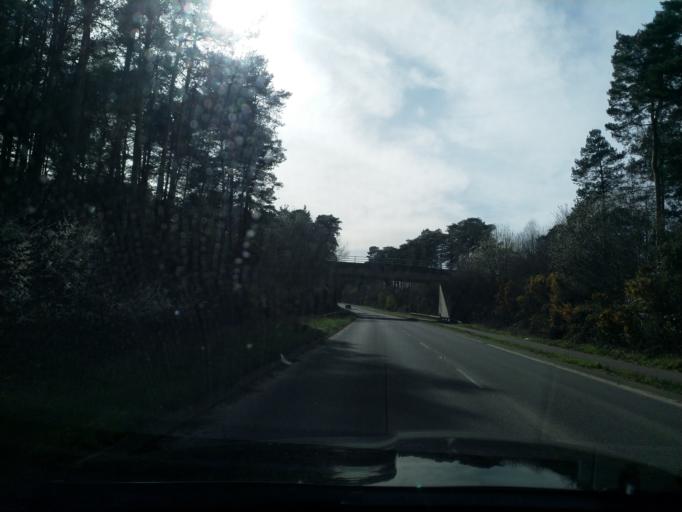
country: GB
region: England
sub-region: Hampshire
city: Fleet
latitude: 51.2825
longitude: -0.7998
